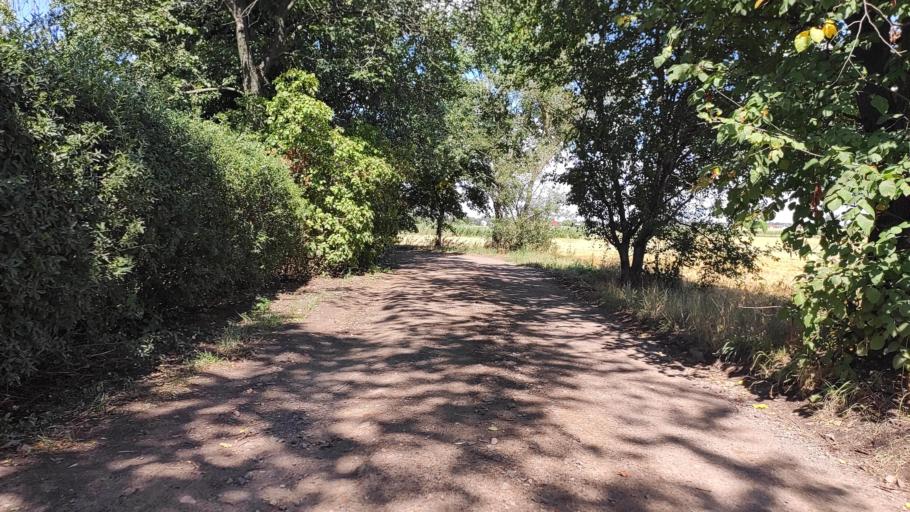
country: PL
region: Greater Poland Voivodeship
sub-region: Powiat poznanski
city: Kleszczewo
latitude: 52.3850
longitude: 17.1503
